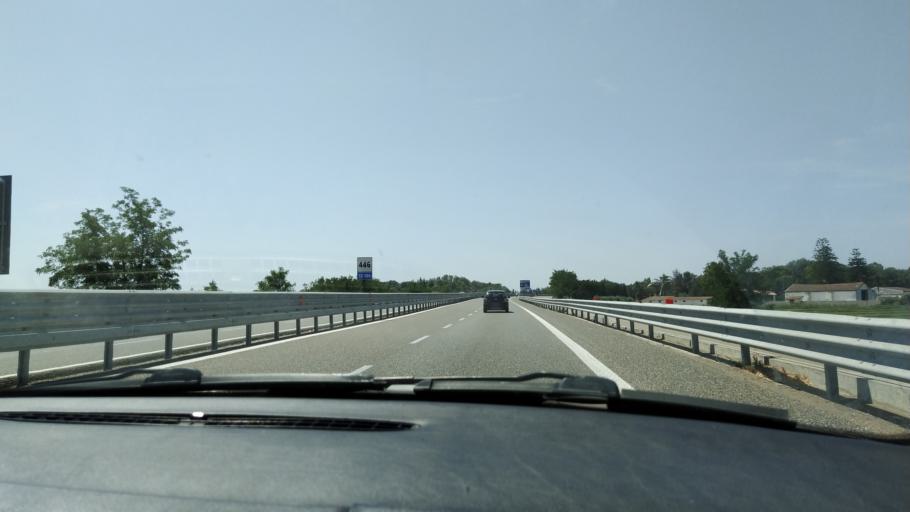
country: IT
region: Basilicate
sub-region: Provincia di Matera
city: Marconia
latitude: 40.3700
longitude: 16.7840
